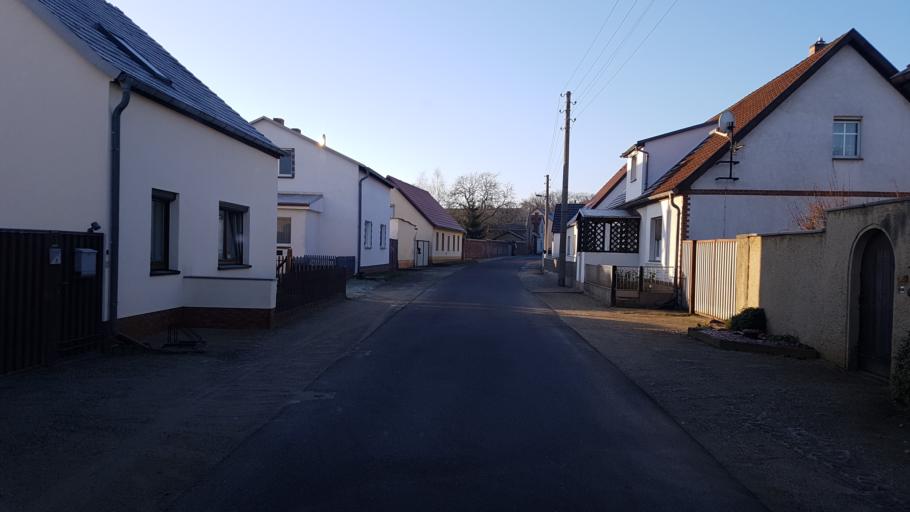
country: DE
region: Brandenburg
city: Sallgast
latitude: 51.5909
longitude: 13.8475
